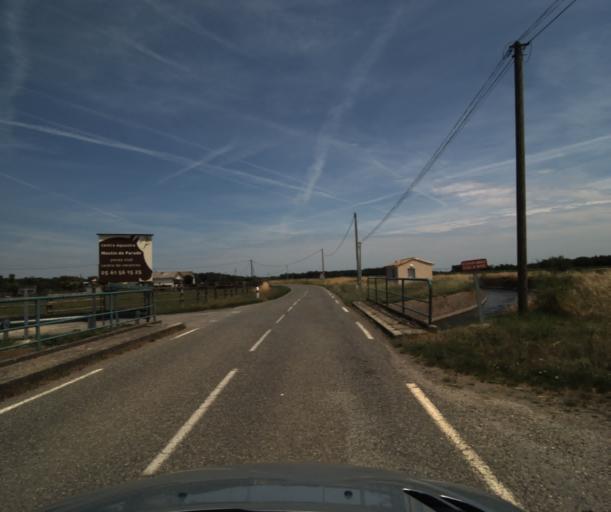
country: FR
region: Midi-Pyrenees
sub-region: Departement de la Haute-Garonne
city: Lherm
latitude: 43.4403
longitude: 1.2268
